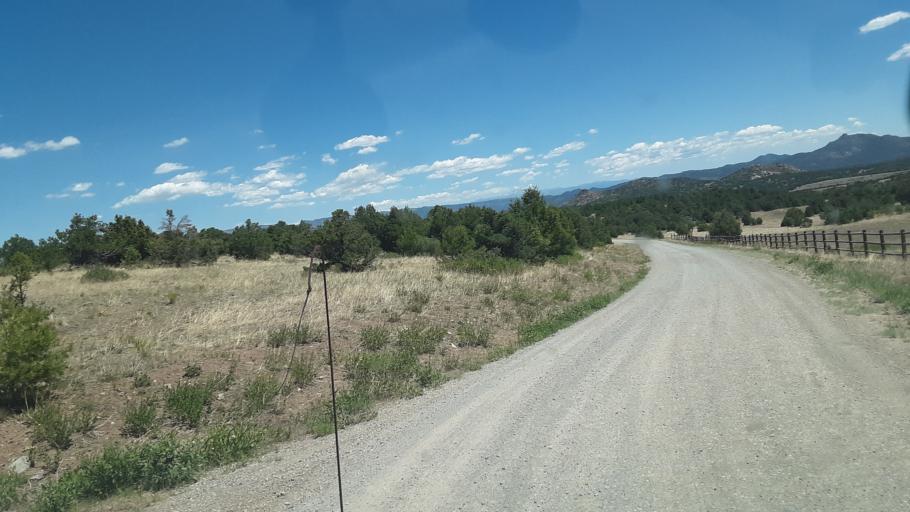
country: US
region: Colorado
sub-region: Custer County
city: Westcliffe
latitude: 38.3071
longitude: -105.6776
